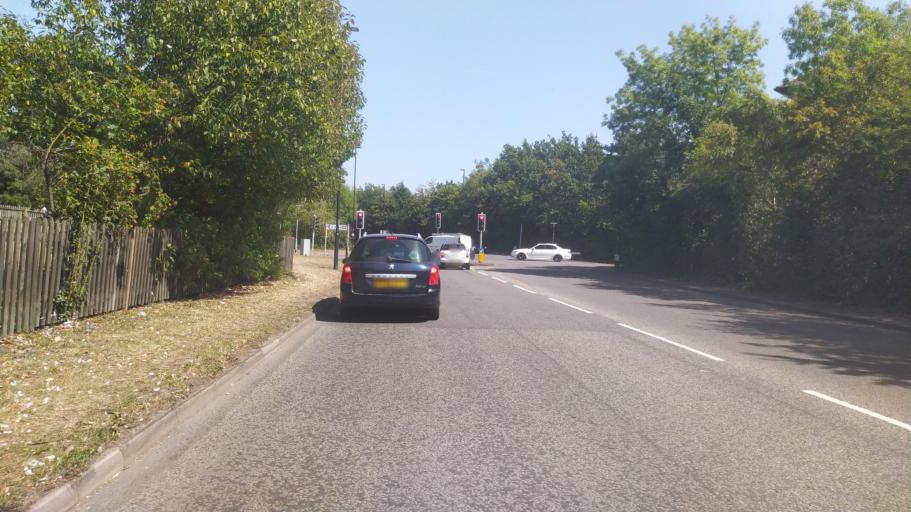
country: GB
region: England
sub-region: Southampton
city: Southampton
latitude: 50.9202
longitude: -1.3913
